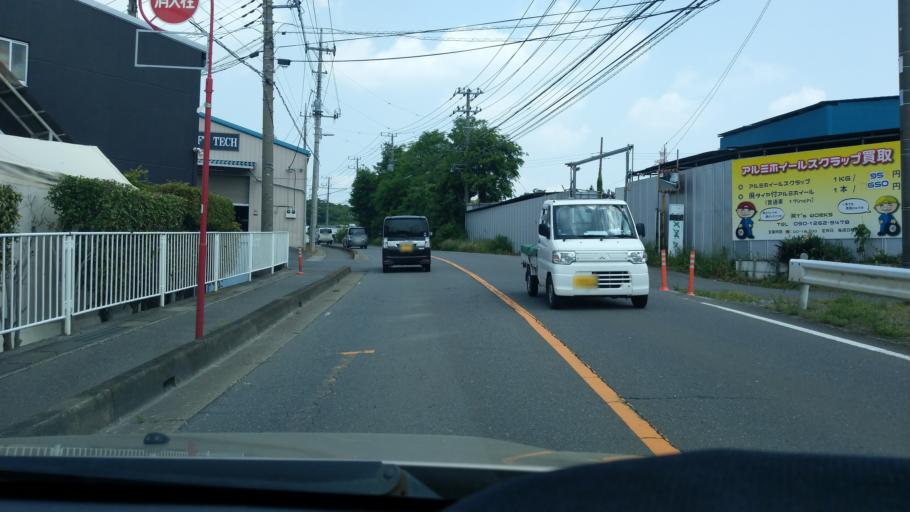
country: JP
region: Saitama
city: Iwatsuki
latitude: 35.9166
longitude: 139.7164
